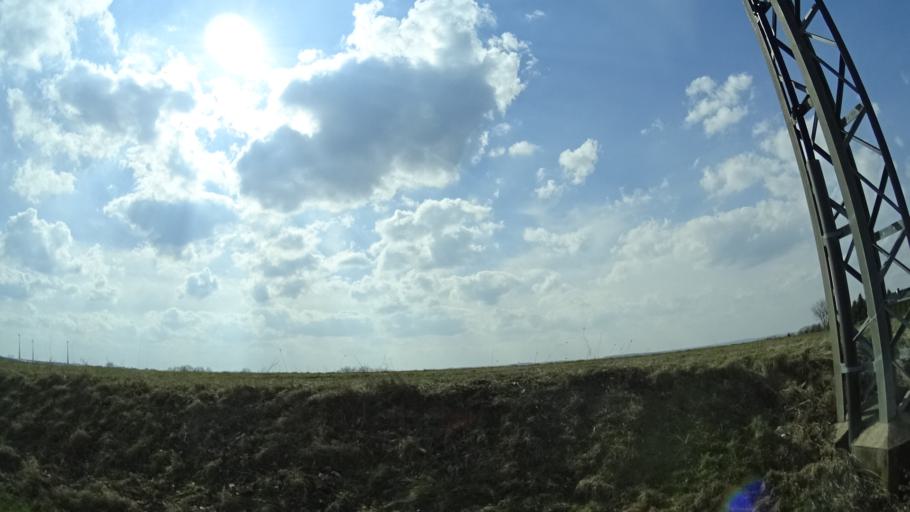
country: DE
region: Saxony-Anhalt
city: Stossen
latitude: 51.1295
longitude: 11.9267
